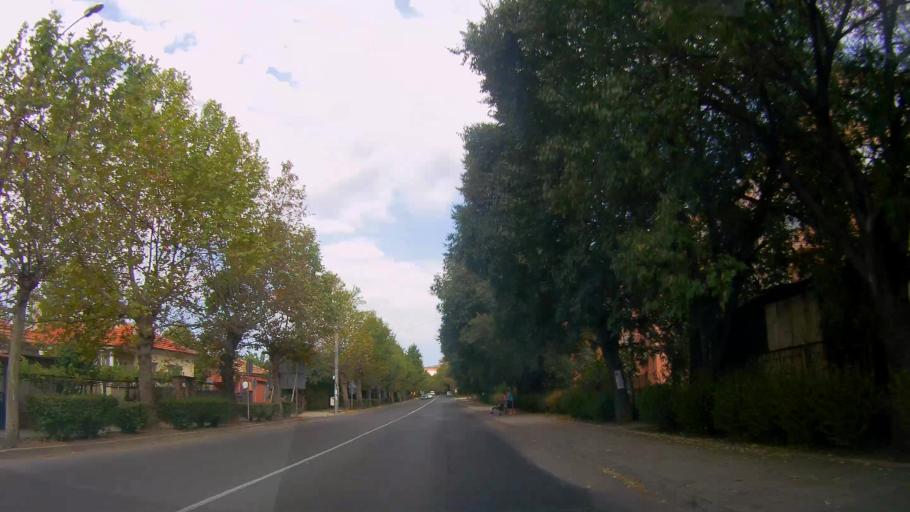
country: BG
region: Burgas
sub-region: Obshtina Aytos
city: Aytos
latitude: 42.6997
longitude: 27.2483
